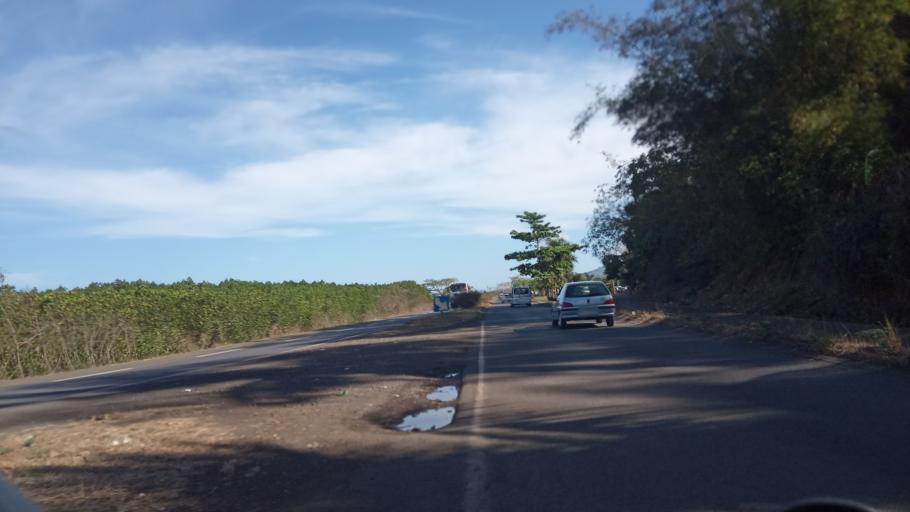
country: YT
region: Mamoudzou
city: Mamoudzou
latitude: -12.7980
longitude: 45.2158
